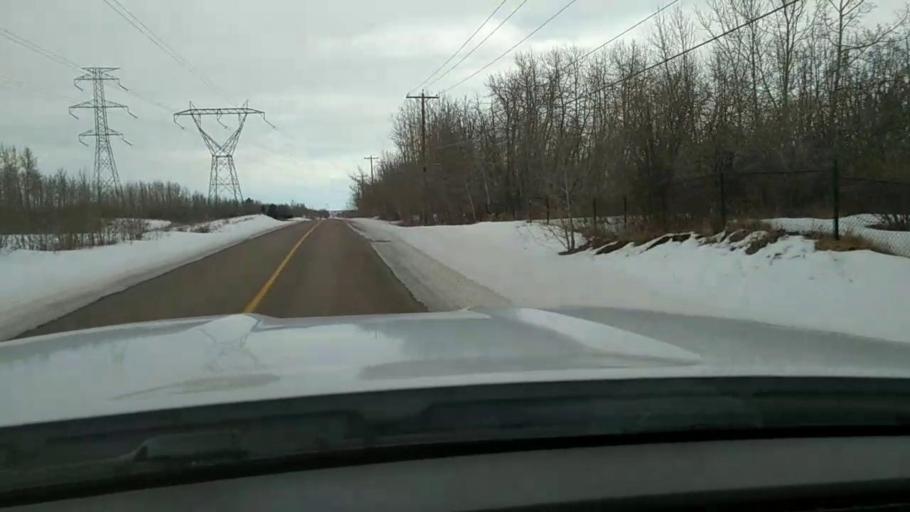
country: CA
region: Alberta
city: Cochrane
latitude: 51.1795
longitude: -114.2575
